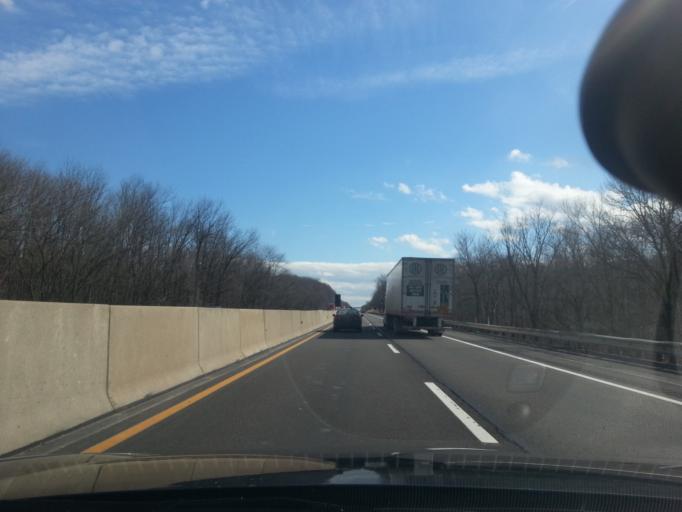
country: US
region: Pennsylvania
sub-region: Montgomery County
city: Woxall
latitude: 40.3687
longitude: -75.4008
